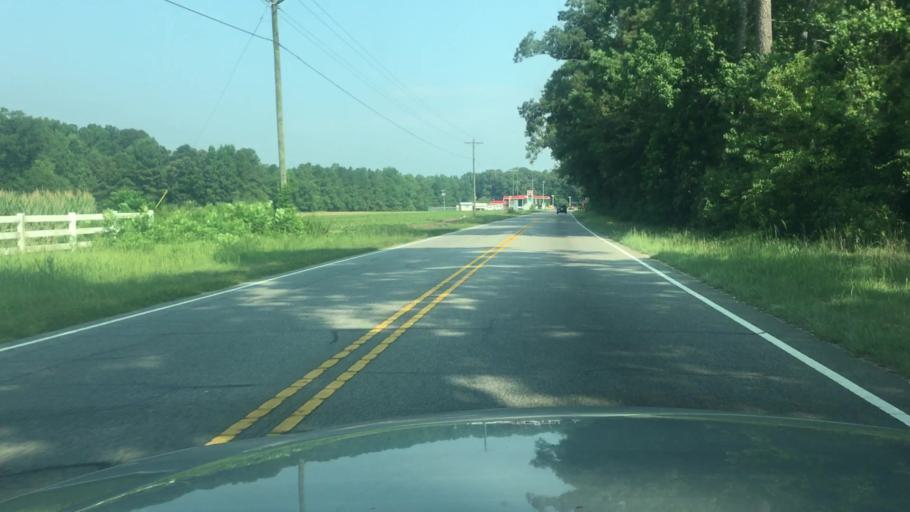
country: US
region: North Carolina
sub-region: Cumberland County
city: Hope Mills
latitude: 34.9323
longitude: -78.9175
